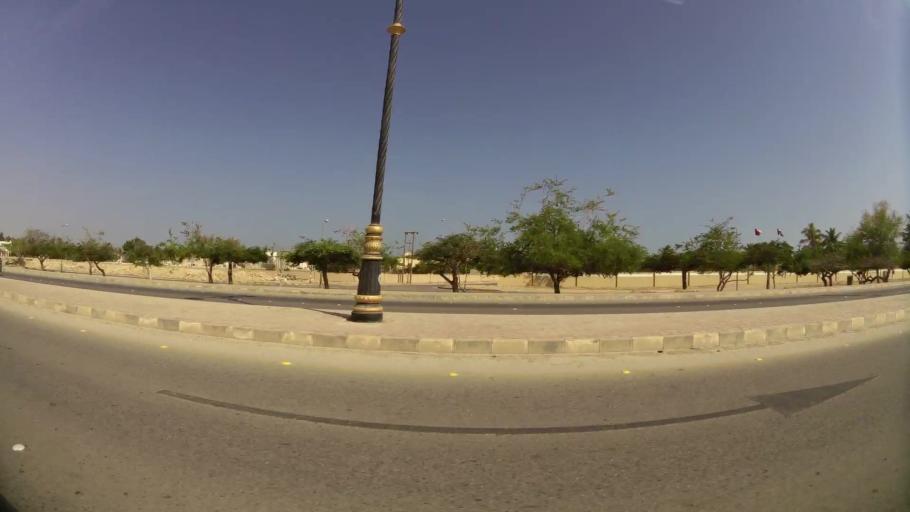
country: OM
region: Zufar
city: Salalah
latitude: 17.0121
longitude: 54.0485
